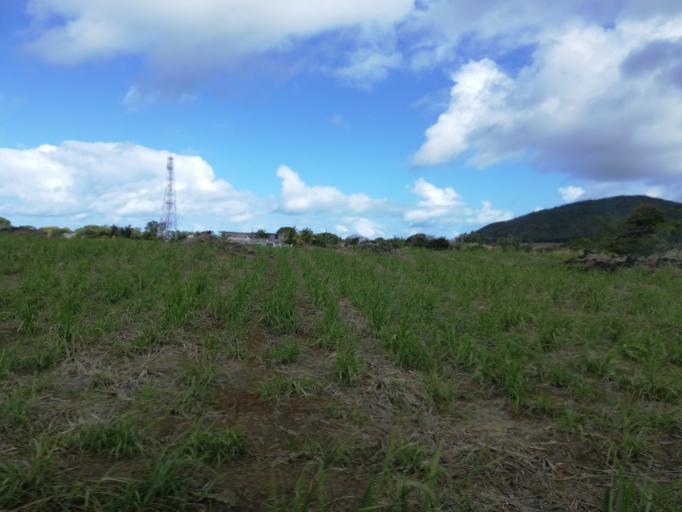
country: MU
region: Flacq
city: Grande Riviere Sud Est
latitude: -20.2732
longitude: 57.7698
